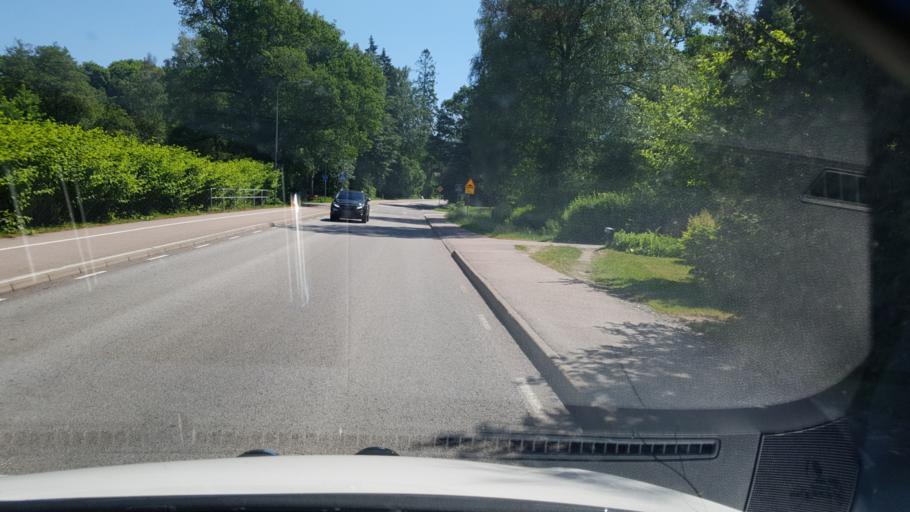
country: SE
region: Vaestra Goetaland
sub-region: Lerums Kommun
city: Stenkullen
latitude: 57.8052
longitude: 12.3625
